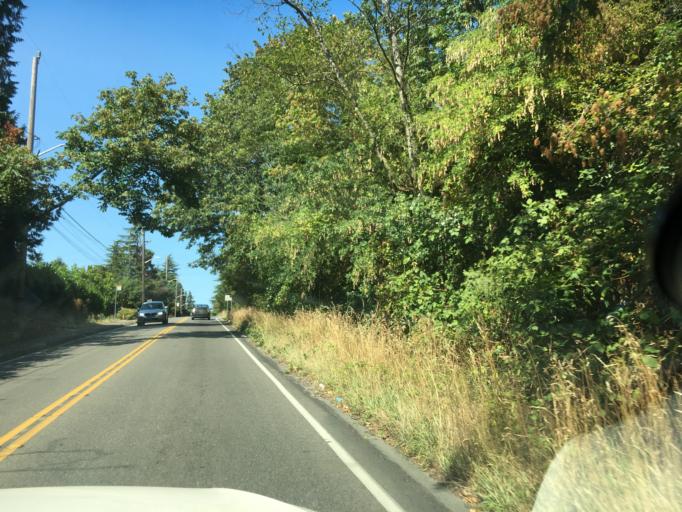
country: US
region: Washington
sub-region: King County
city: Shoreline
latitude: 47.7134
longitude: -122.3609
